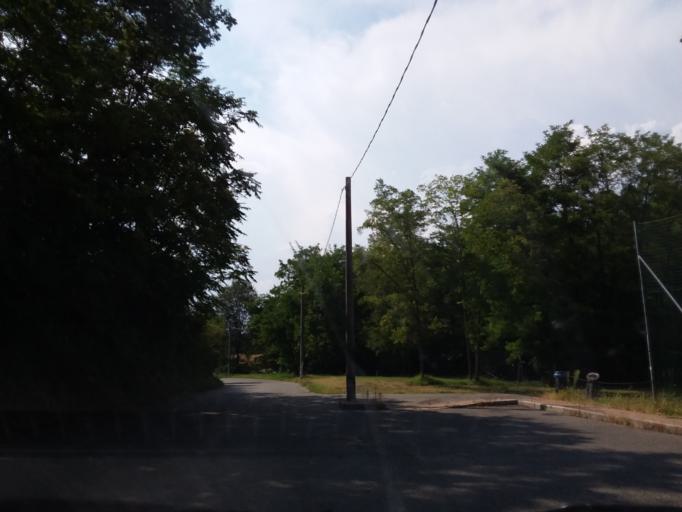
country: IT
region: Piedmont
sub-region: Provincia di Torino
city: Pianezza
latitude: 45.0859
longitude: 7.5445
